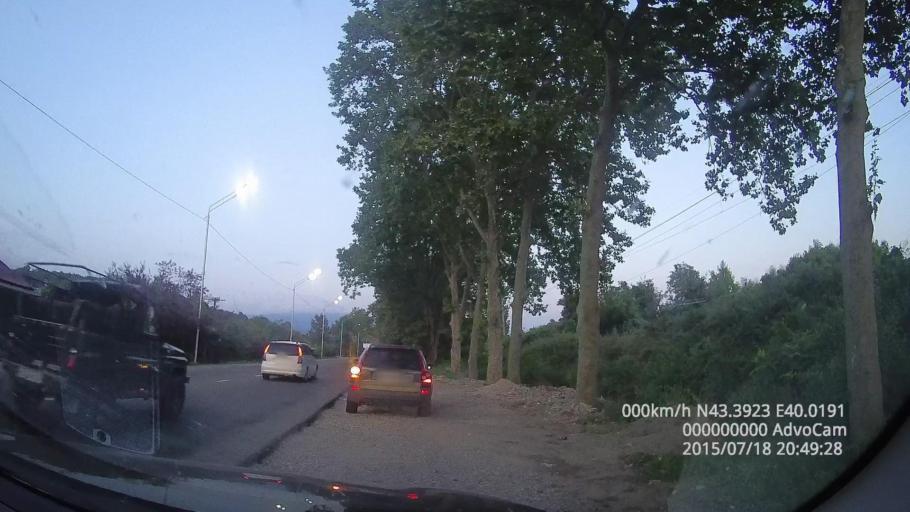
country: GE
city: Gantiadi
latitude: 43.3922
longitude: 40.0192
